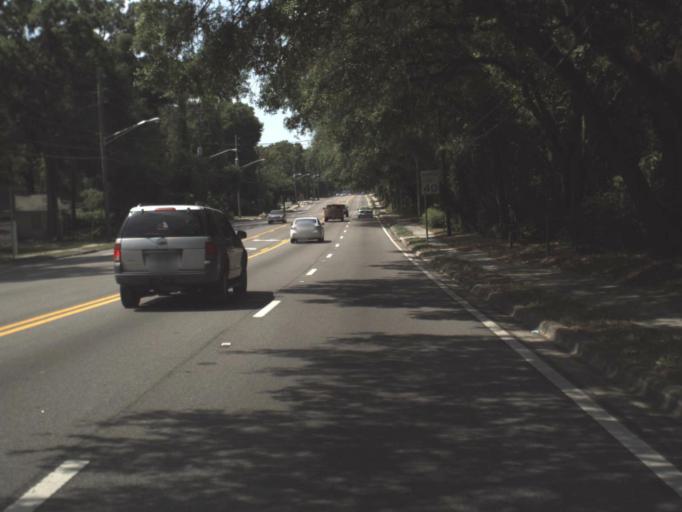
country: US
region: Florida
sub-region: Duval County
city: Jacksonville
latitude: 30.3089
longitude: -81.6002
